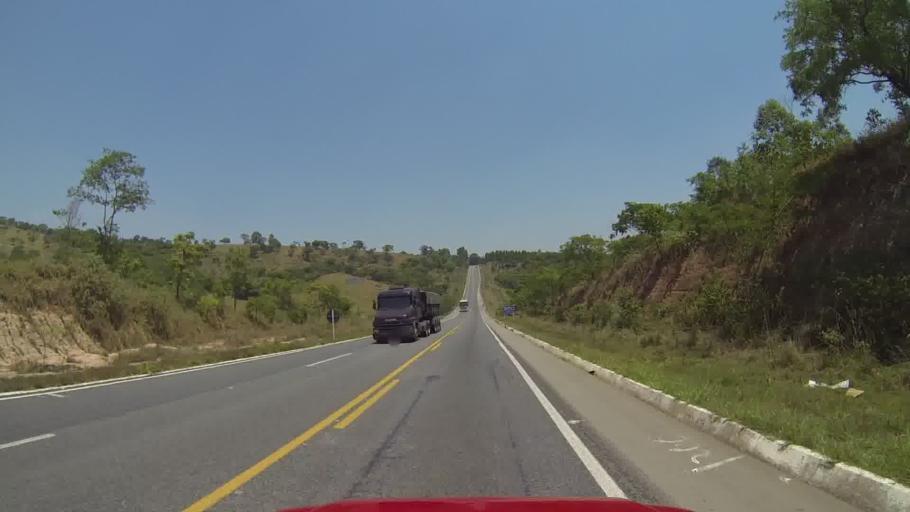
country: BR
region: Minas Gerais
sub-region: Itapecerica
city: Itapecerica
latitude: -20.2768
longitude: -45.1233
